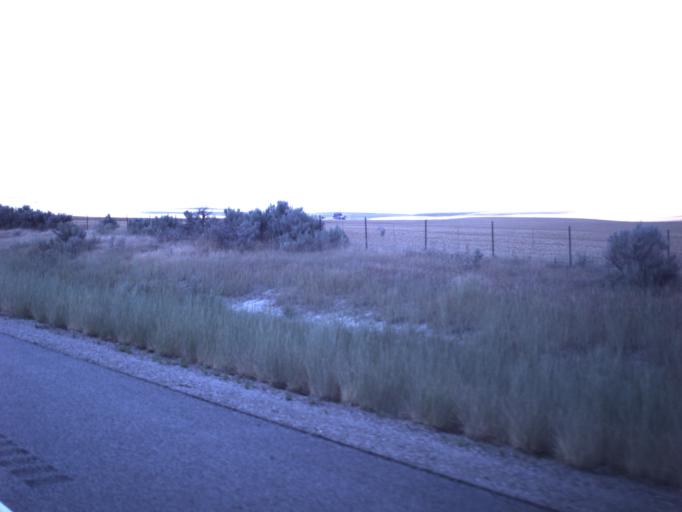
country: US
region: Utah
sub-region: Box Elder County
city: Garland
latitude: 41.8887
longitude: -112.5037
